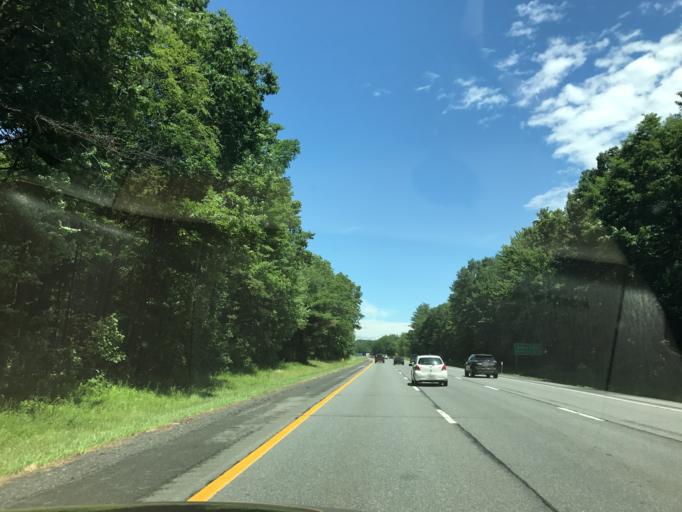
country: US
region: New York
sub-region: Warren County
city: West Glens Falls
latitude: 43.1973
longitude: -73.6999
